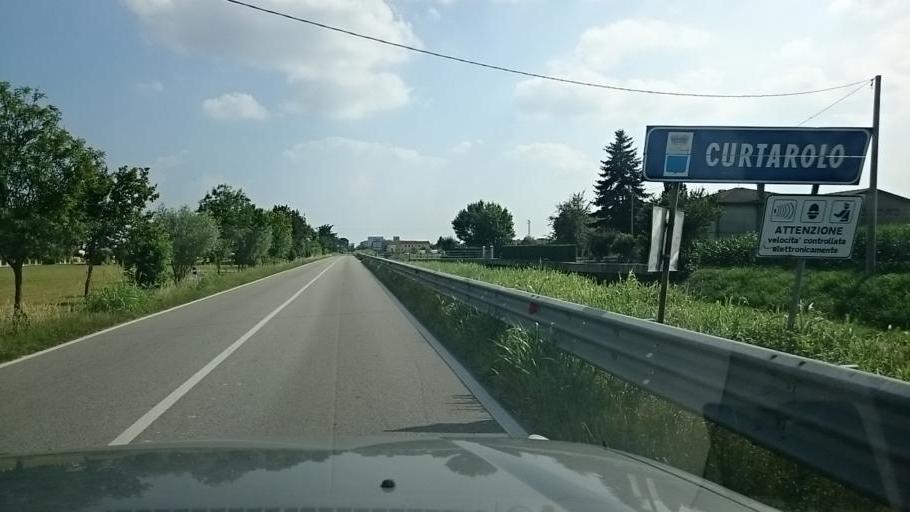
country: IT
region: Veneto
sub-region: Provincia di Padova
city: Cavino
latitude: 45.5269
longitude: 11.8692
